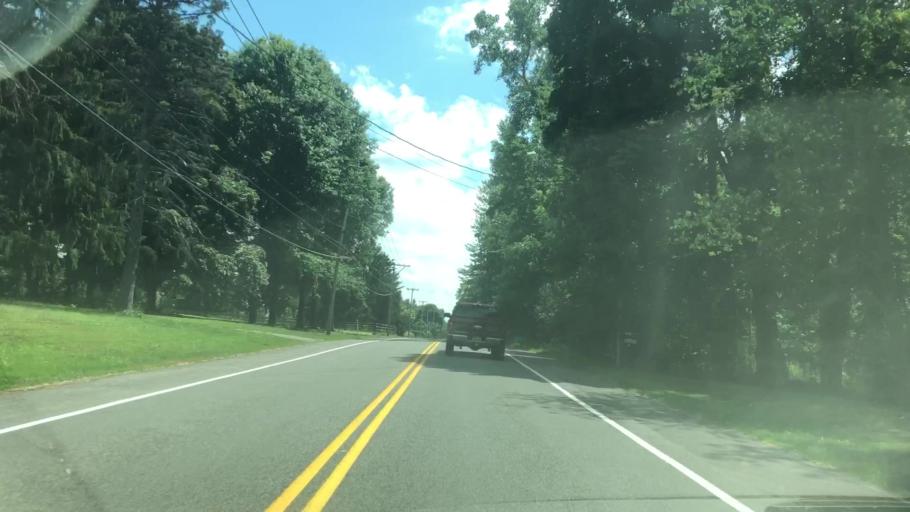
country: US
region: New York
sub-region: Monroe County
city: Fairport
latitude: 43.1335
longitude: -77.4005
